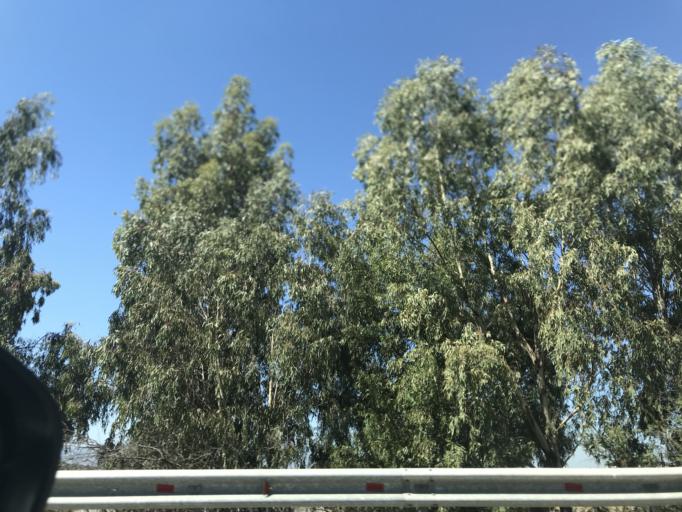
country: TR
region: Aydin
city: Aydin
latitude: 37.8178
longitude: 27.8443
